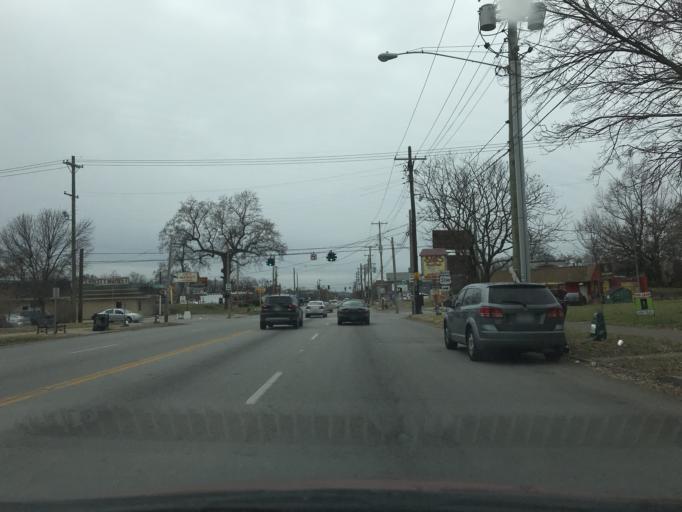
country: US
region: Kentucky
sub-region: Jefferson County
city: Louisville
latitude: 38.2492
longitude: -85.7859
